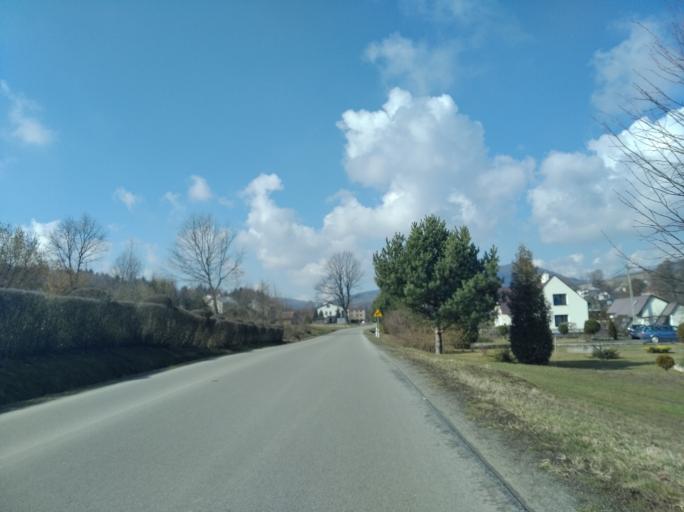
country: PL
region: Subcarpathian Voivodeship
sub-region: Powiat strzyzowski
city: Frysztak
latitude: 49.8709
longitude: 21.5979
